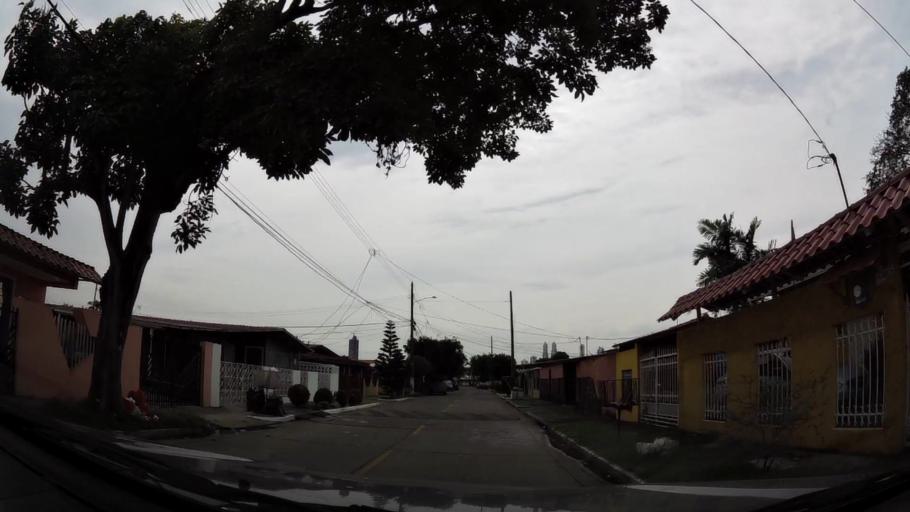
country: PA
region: Panama
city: San Miguelito
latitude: 9.0351
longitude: -79.4764
